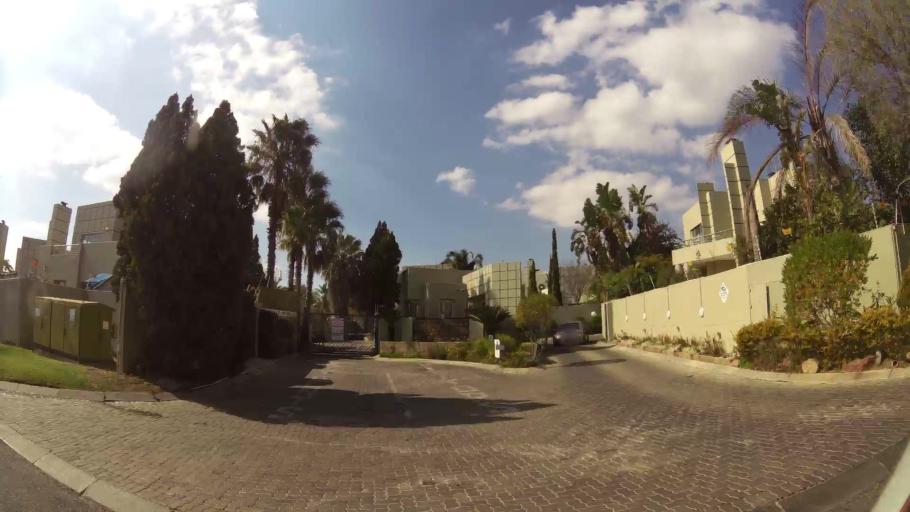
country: ZA
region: Gauteng
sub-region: City of Johannesburg Metropolitan Municipality
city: Midrand
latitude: -26.0262
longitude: 28.0753
